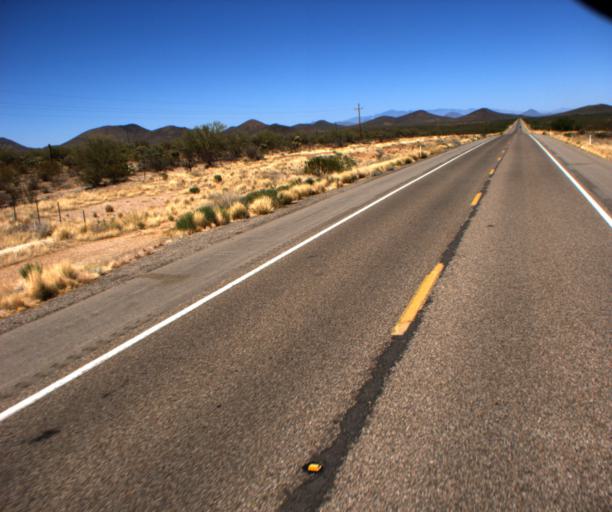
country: US
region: Arizona
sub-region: Pima County
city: Three Points
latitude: 32.0456
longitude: -111.4326
